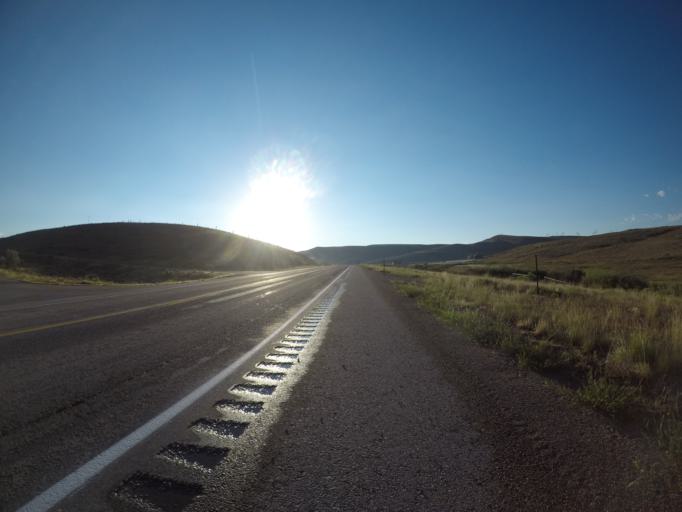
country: US
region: Wyoming
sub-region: Lincoln County
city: Kemmerer
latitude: 41.8695
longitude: -110.5020
